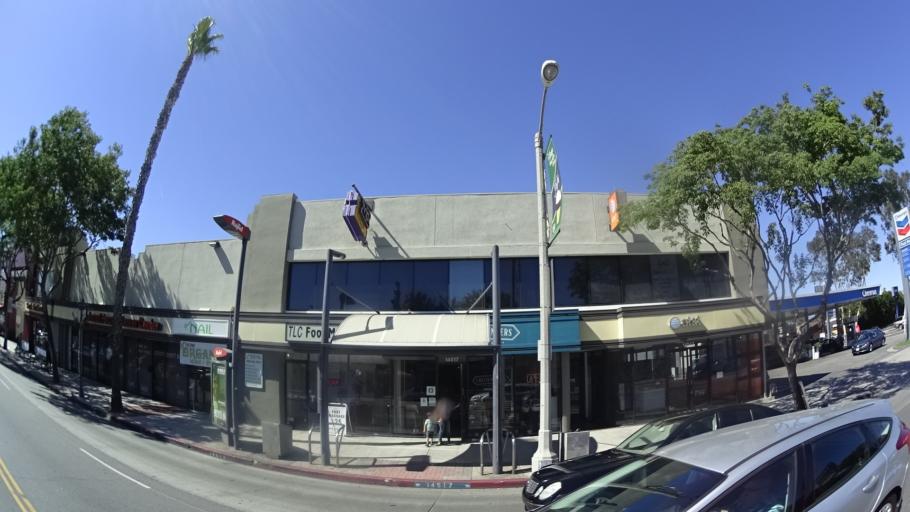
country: US
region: California
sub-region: Los Angeles County
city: Sherman Oaks
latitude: 34.1511
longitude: -118.4494
